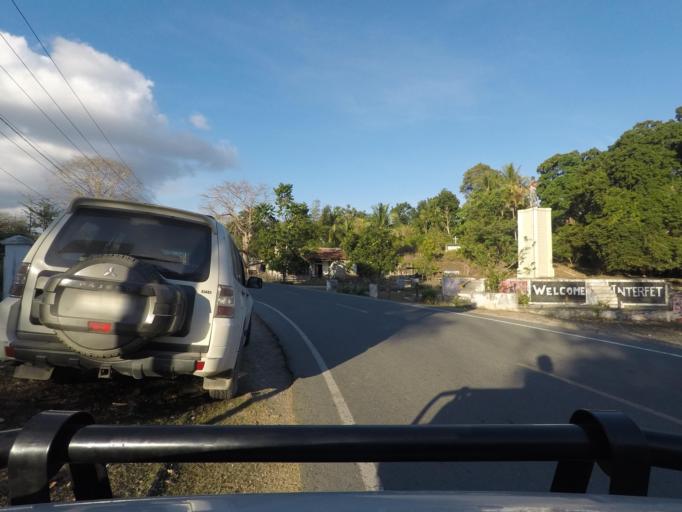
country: TL
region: Bobonaro
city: Maliana
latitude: -8.9661
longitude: 125.0473
